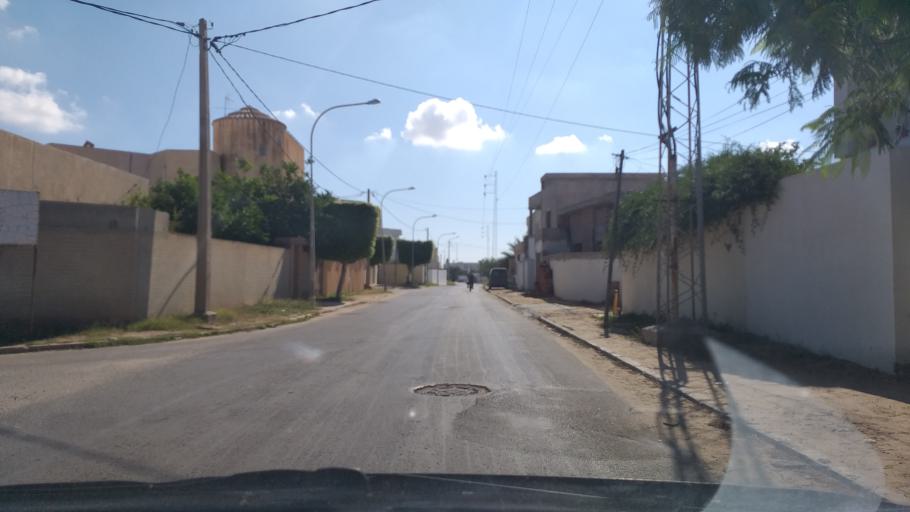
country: TN
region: Safaqis
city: Al Qarmadah
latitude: 34.8036
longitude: 10.7701
